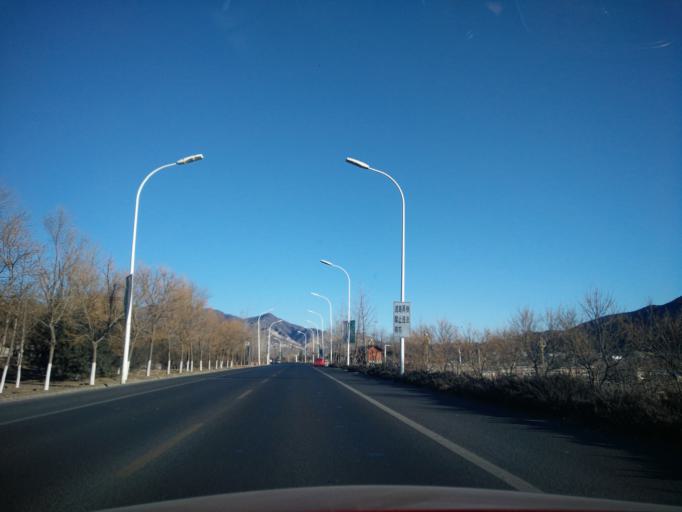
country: CN
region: Beijing
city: Chengzi
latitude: 39.9733
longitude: 116.0854
